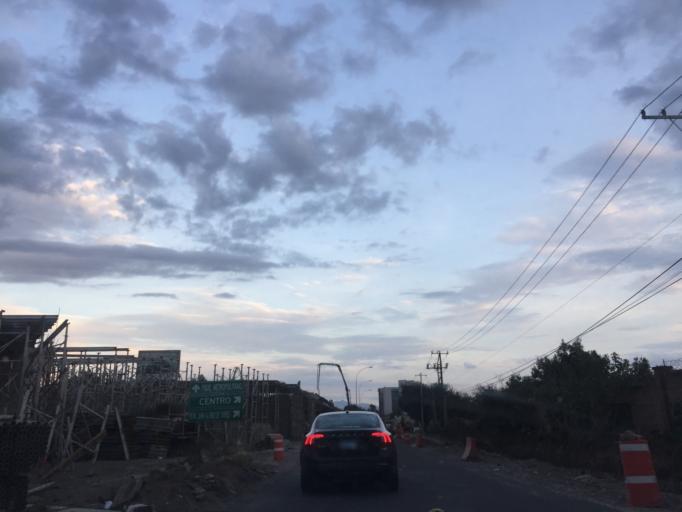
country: MX
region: Guanajuato
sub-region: Leon
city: La Ermita
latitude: 21.1702
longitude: -101.6987
